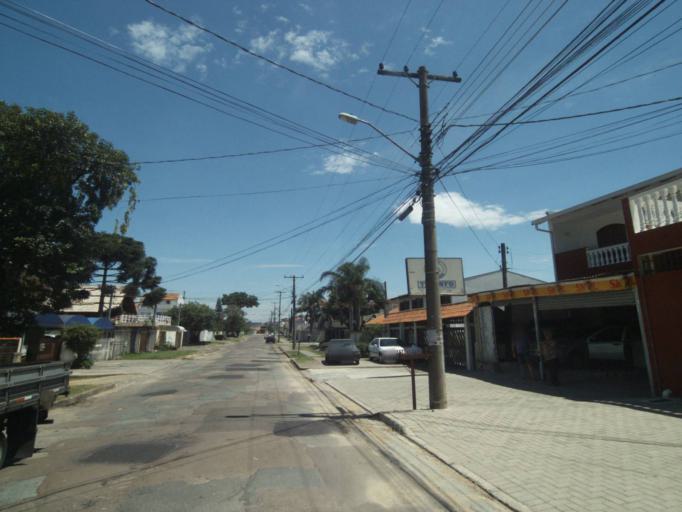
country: BR
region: Parana
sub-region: Curitiba
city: Curitiba
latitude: -25.4731
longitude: -49.2410
